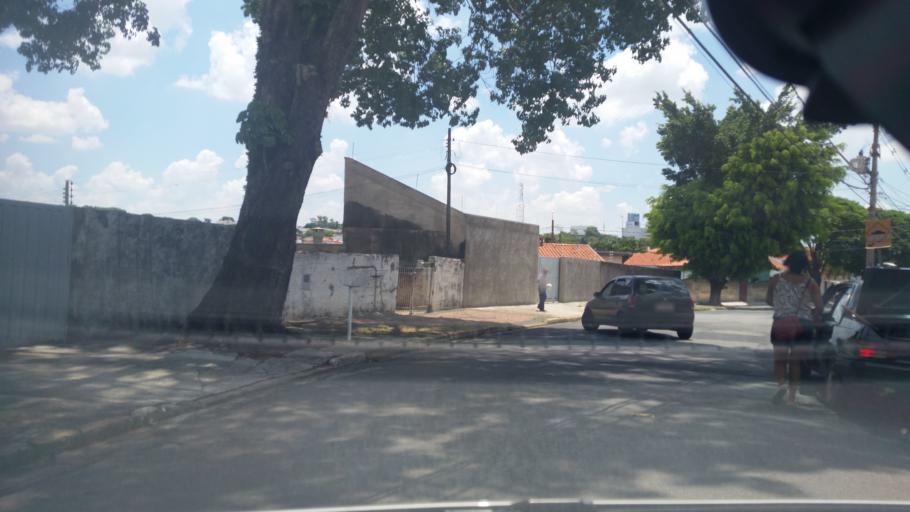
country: BR
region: Sao Paulo
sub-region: Campinas
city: Campinas
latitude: -22.8568
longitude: -47.0385
